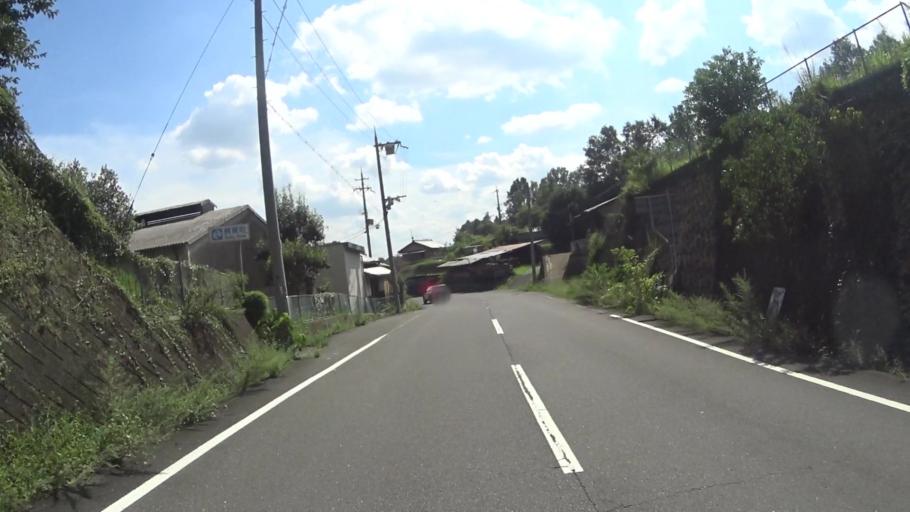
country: JP
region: Kyoto
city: Tanabe
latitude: 34.7528
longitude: 135.7379
